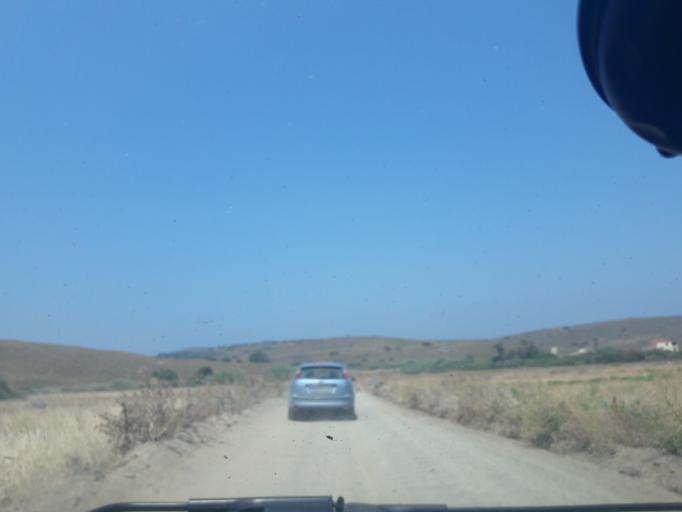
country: GR
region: North Aegean
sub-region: Nomos Lesvou
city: Myrina
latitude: 39.9812
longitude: 25.1483
